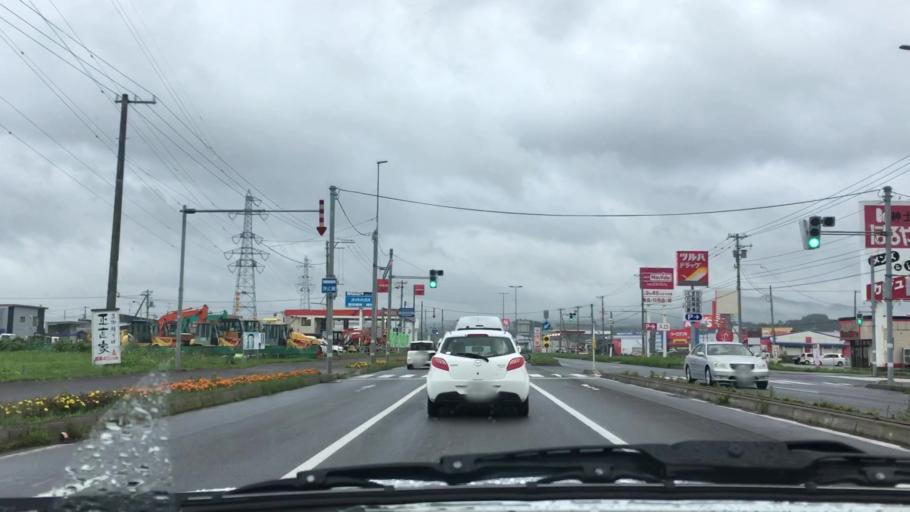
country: JP
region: Hokkaido
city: Nanae
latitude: 42.2525
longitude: 140.2843
